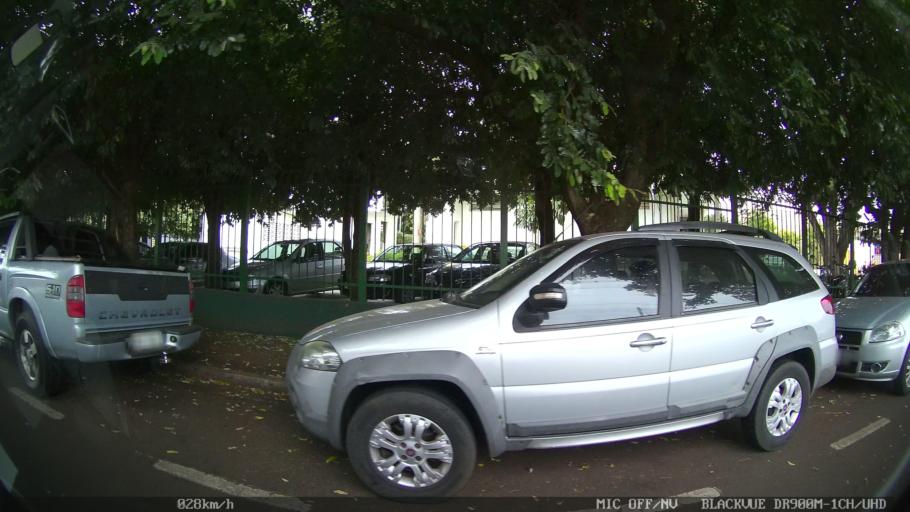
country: BR
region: Sao Paulo
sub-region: Sao Jose Do Rio Preto
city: Sao Jose do Rio Preto
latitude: -20.8279
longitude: -49.3940
